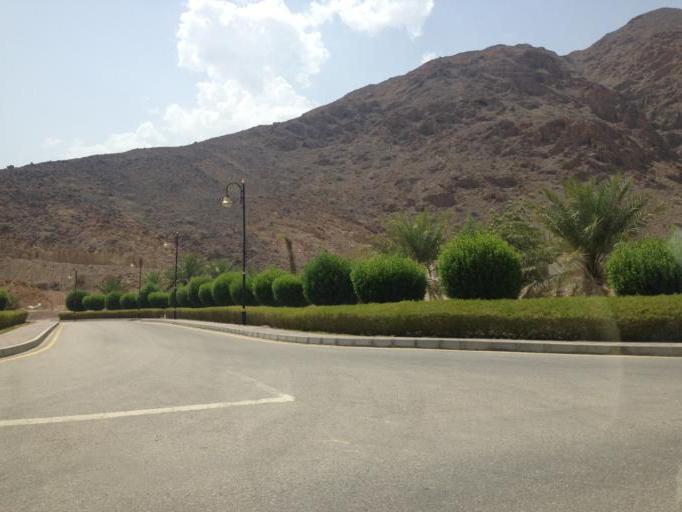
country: OM
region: Ash Sharqiyah
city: Ibra'
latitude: 23.0923
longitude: 58.8506
